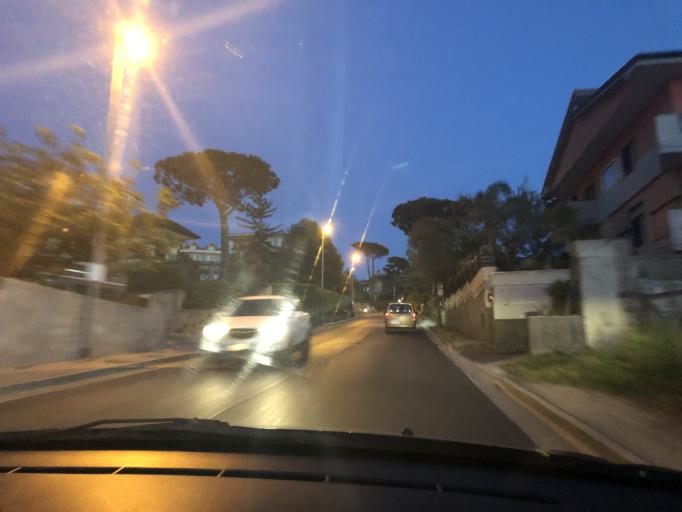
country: IT
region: Campania
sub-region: Provincia di Napoli
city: Marano di Napoli
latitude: 40.8882
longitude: 14.1797
